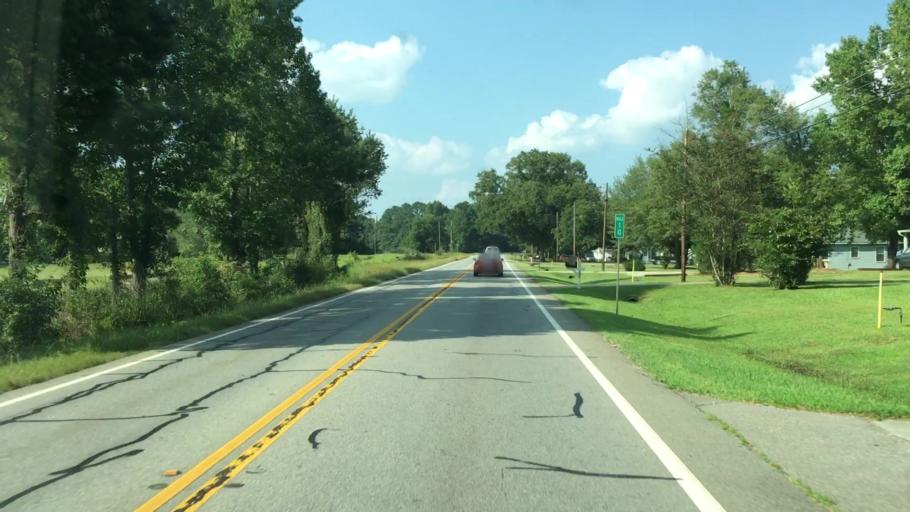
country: US
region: Georgia
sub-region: Walton County
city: Monroe
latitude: 33.7495
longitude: -83.7023
